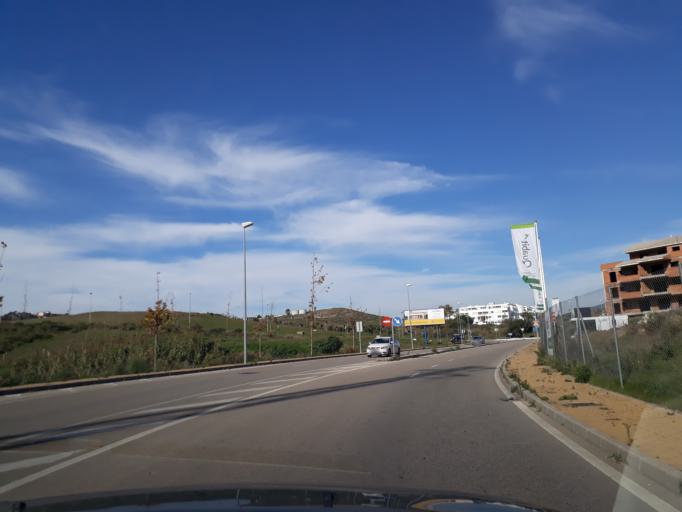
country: ES
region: Andalusia
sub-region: Provincia de Malaga
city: Fuengirola
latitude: 36.5237
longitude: -4.6865
